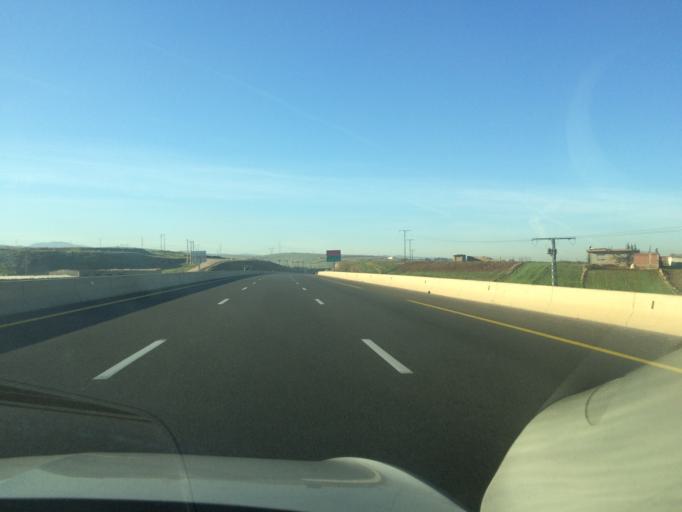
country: DZ
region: Chlef
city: Oued Sly
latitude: 36.0808
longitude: 1.1847
